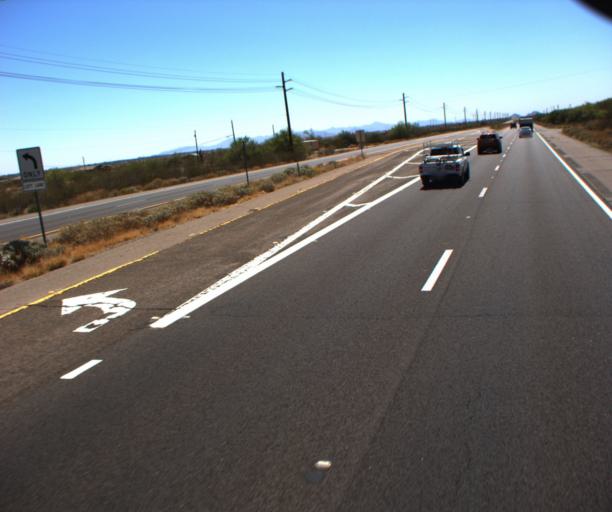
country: US
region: Arizona
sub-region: Maricopa County
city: Mesa
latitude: 33.5088
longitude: -111.7687
